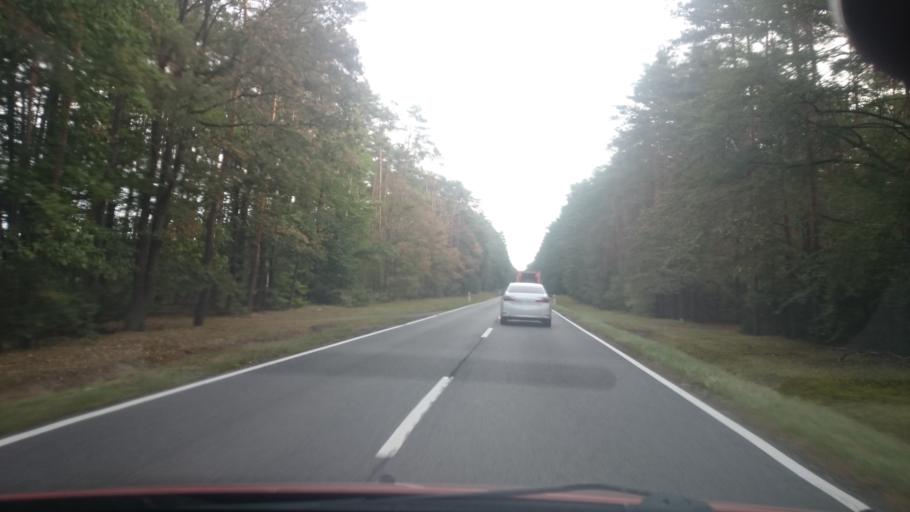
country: PL
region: Lower Silesian Voivodeship
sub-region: Powiat milicki
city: Sulow
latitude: 51.4209
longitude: 17.2391
